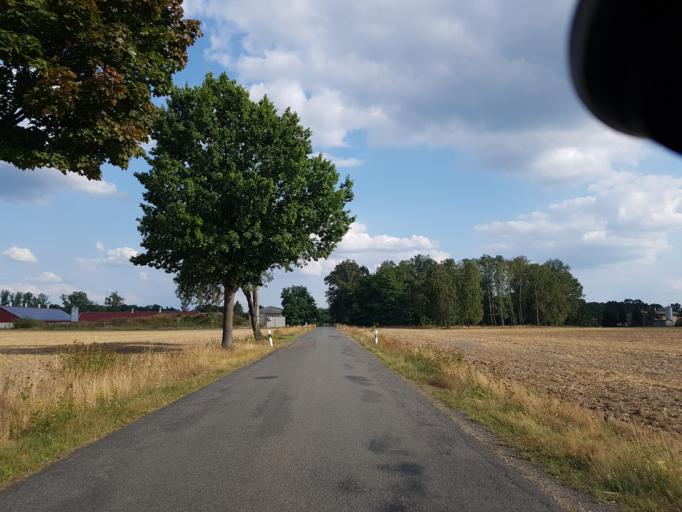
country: DE
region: Brandenburg
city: Bronkow
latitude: 51.6759
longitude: 13.9067
